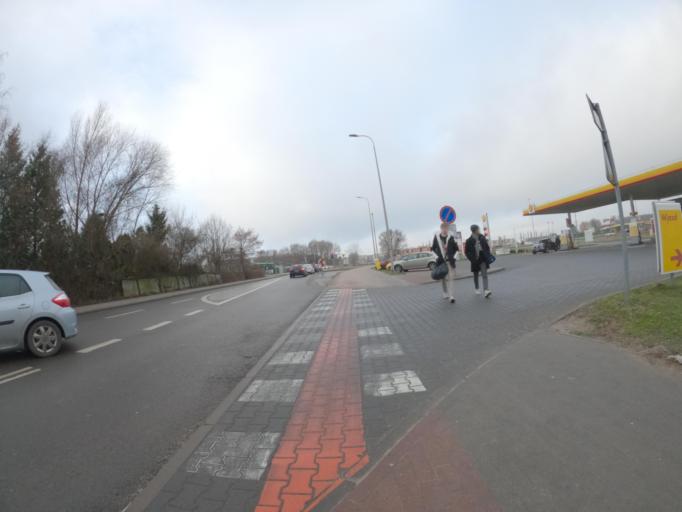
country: PL
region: West Pomeranian Voivodeship
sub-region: Koszalin
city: Koszalin
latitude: 54.2034
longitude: 16.2061
